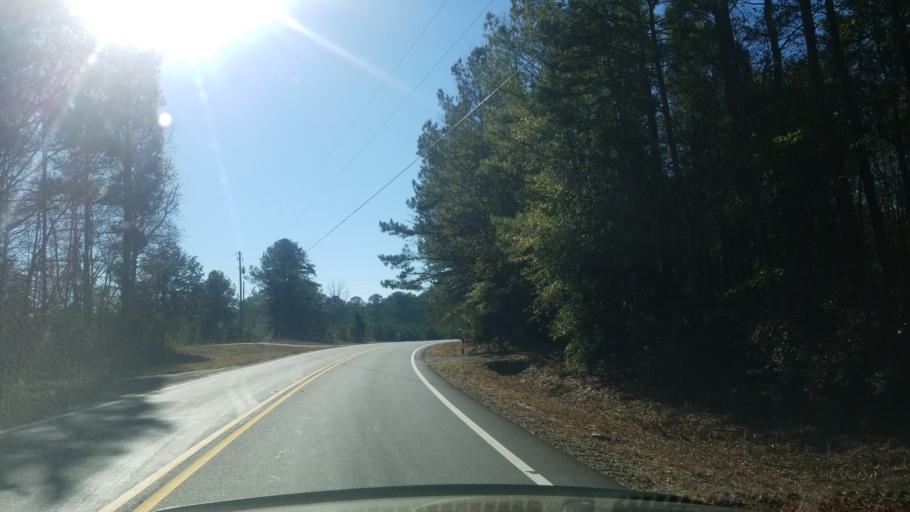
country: US
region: Alabama
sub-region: Chambers County
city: Valley
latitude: 32.8252
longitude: -85.1068
